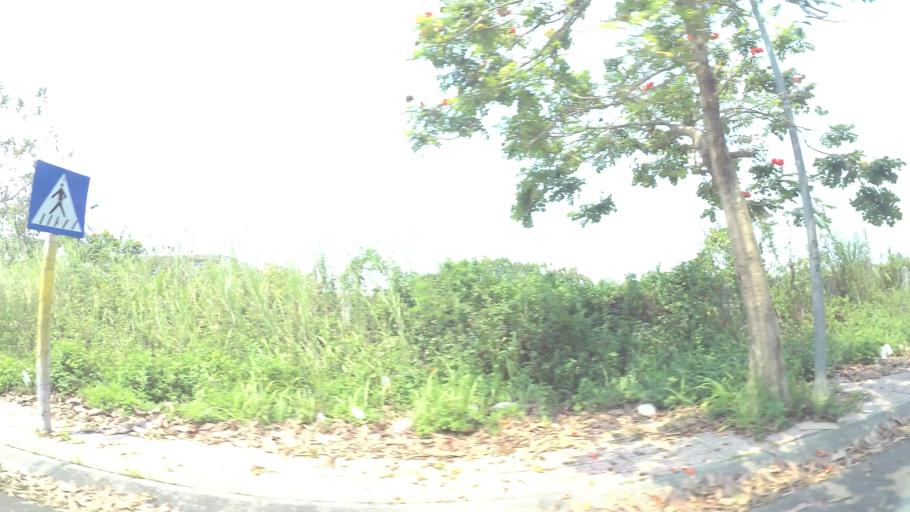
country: VN
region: Da Nang
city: Cam Le
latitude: 16.0146
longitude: 108.2119
